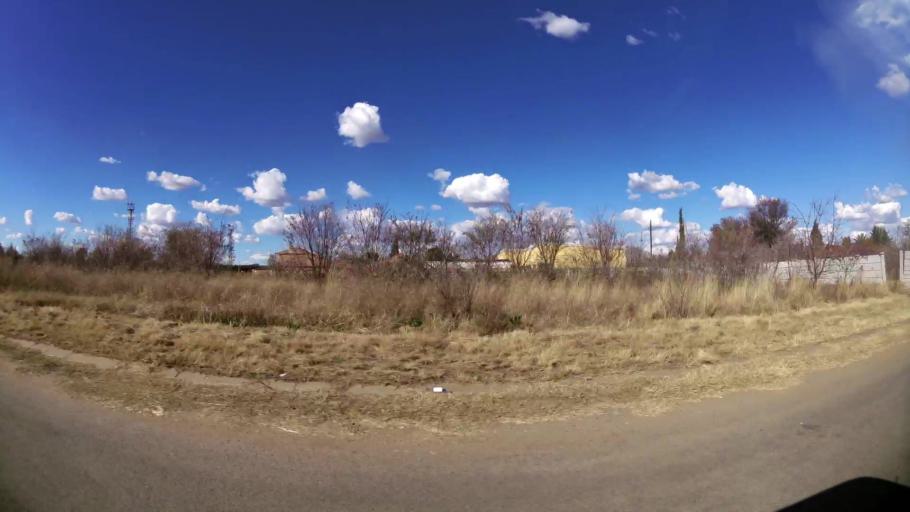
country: ZA
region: North-West
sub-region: Dr Kenneth Kaunda District Municipality
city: Klerksdorp
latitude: -26.8165
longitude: 26.6504
